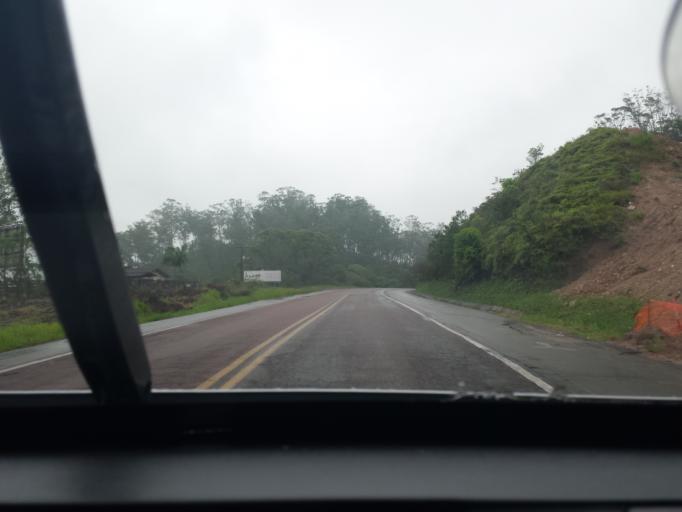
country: BR
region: Santa Catarina
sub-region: Itajai
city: Itajai
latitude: -26.8395
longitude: -48.7811
